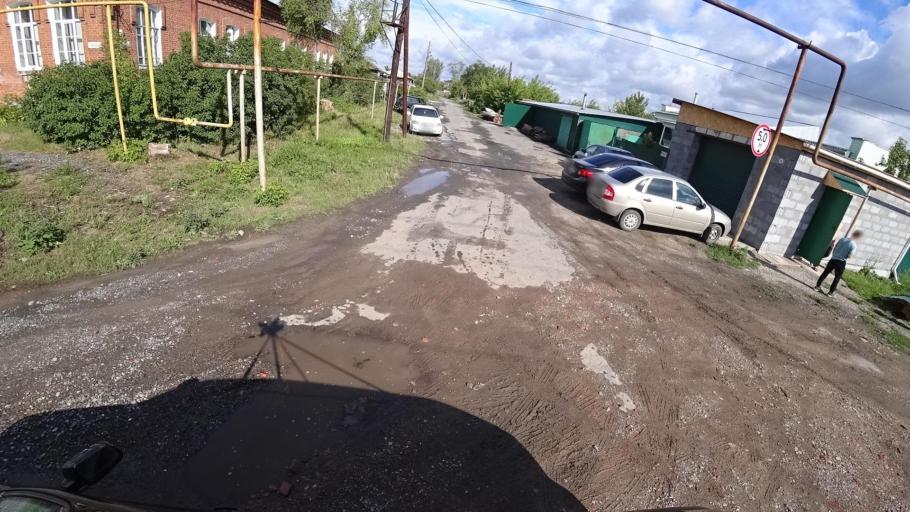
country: RU
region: Sverdlovsk
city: Kamyshlov
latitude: 56.8445
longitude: 62.6910
